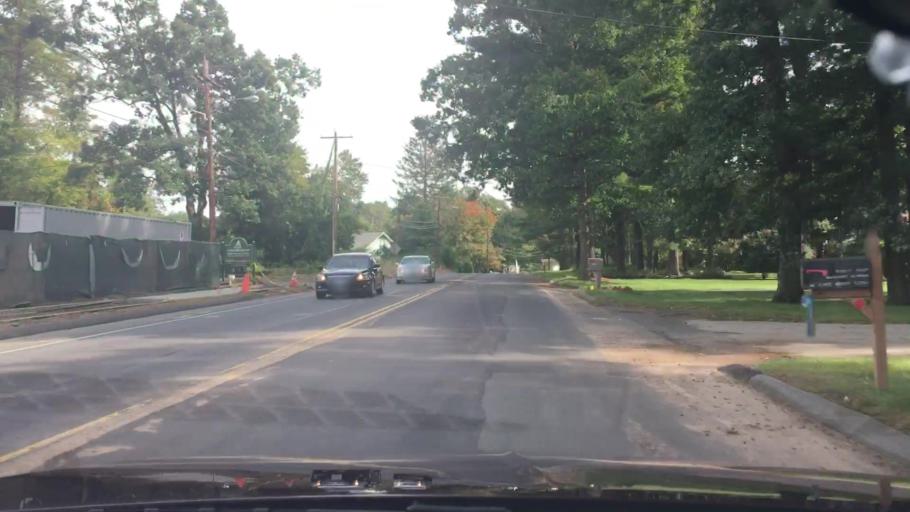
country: US
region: Massachusetts
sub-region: Hampden County
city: East Longmeadow
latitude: 42.0591
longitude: -72.5341
